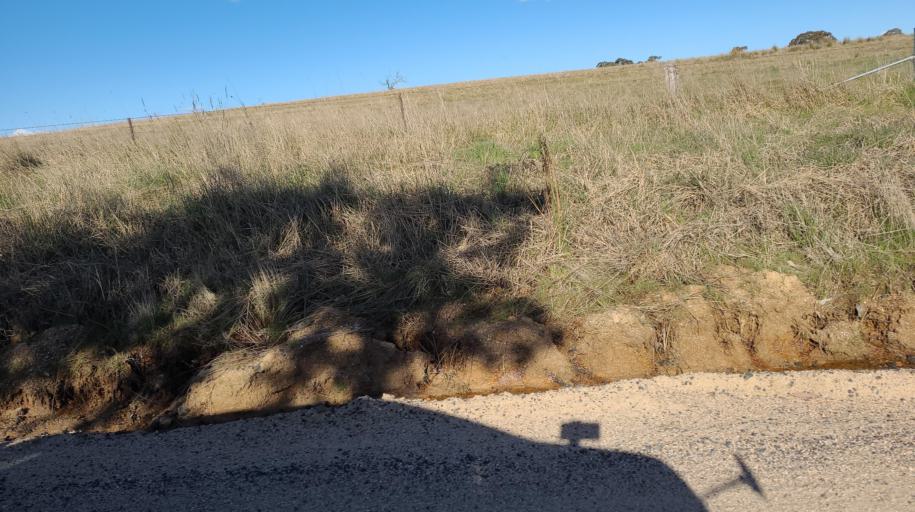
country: AU
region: New South Wales
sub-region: Blayney
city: Millthorpe
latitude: -33.3951
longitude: 149.3095
